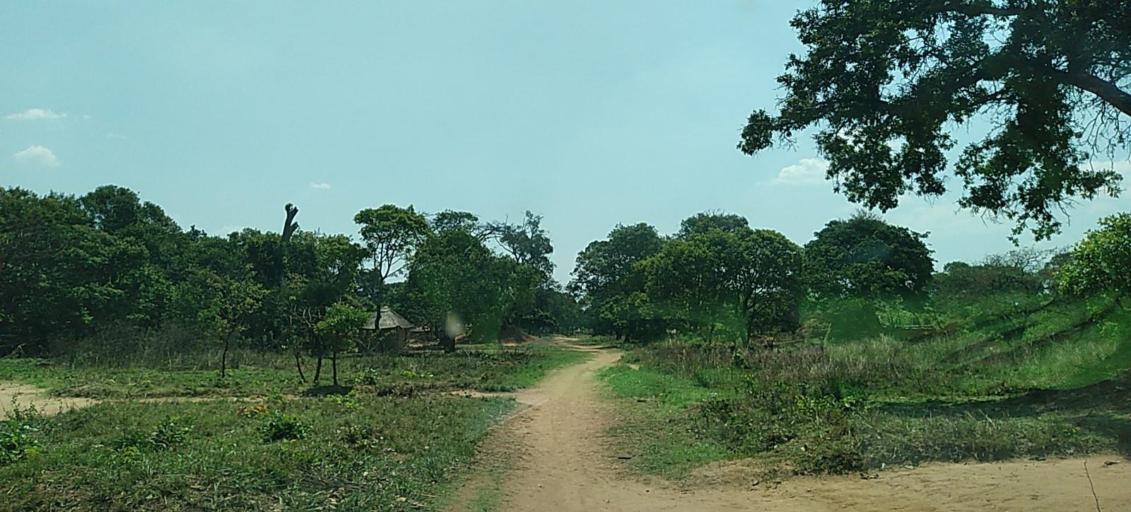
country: CD
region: Katanga
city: Kolwezi
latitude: -11.2786
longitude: 25.1230
